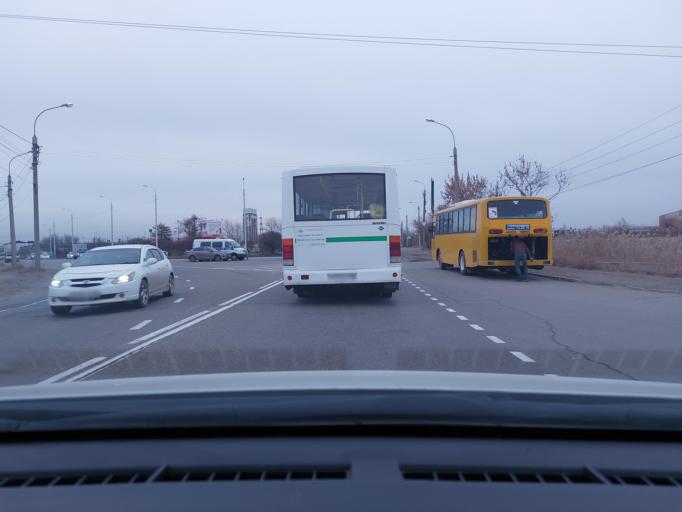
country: RU
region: Irkutsk
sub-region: Irkutskiy Rayon
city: Irkutsk
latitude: 52.3307
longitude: 104.2308
